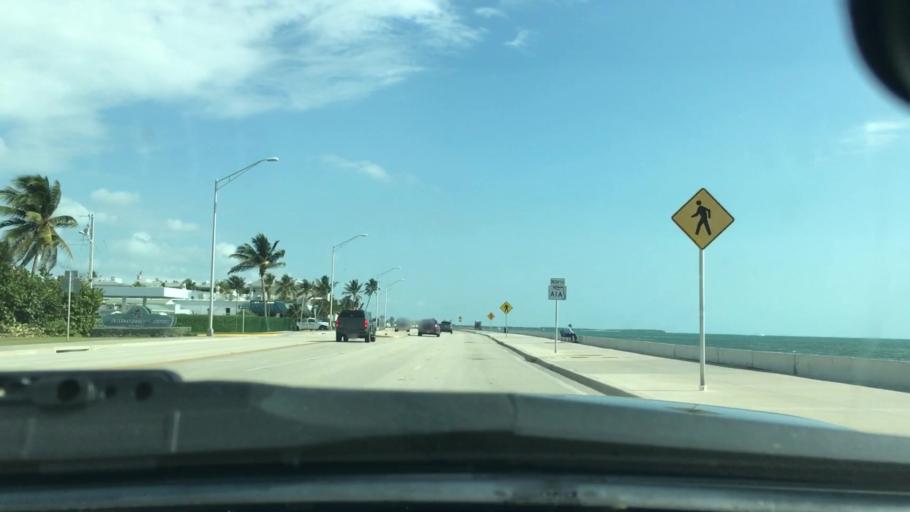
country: US
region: Florida
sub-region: Monroe County
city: Stock Island
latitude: 24.5520
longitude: -81.7541
